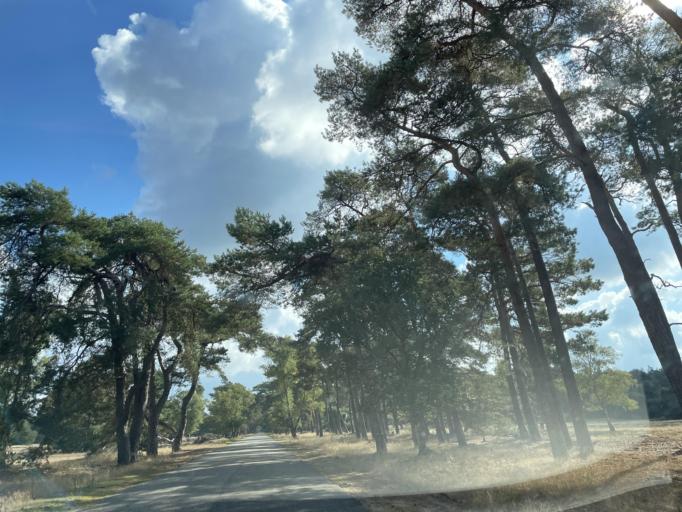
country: NL
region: Gelderland
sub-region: Gemeente Ede
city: Otterlo
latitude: 52.1004
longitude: 5.7983
